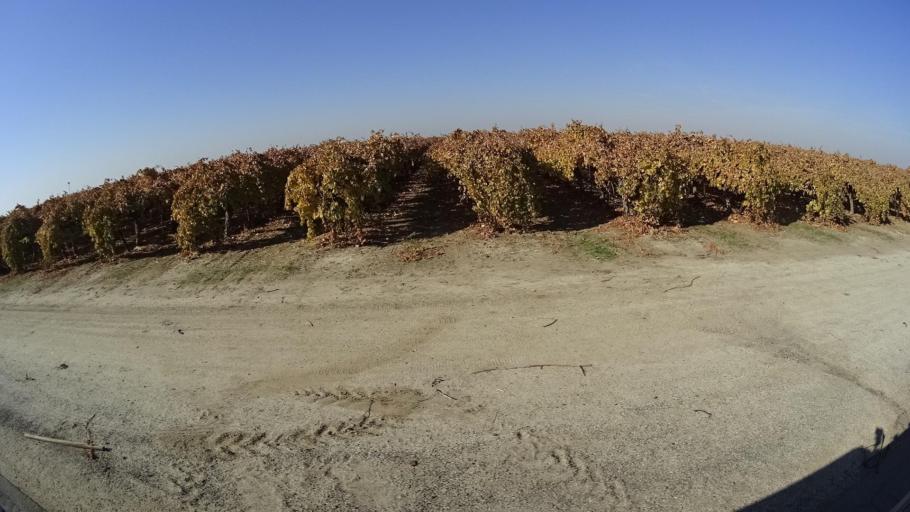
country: US
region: California
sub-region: Kern County
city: McFarland
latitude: 35.7247
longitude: -119.2051
